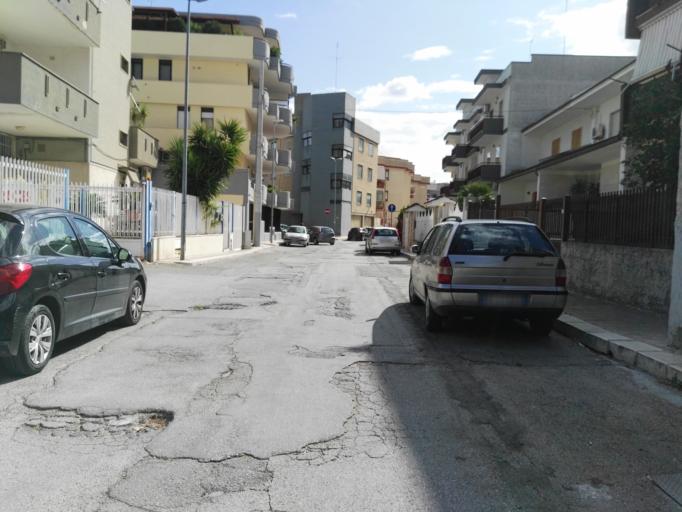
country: IT
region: Apulia
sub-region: Provincia di Bari
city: Triggiano
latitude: 41.0657
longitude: 16.9162
